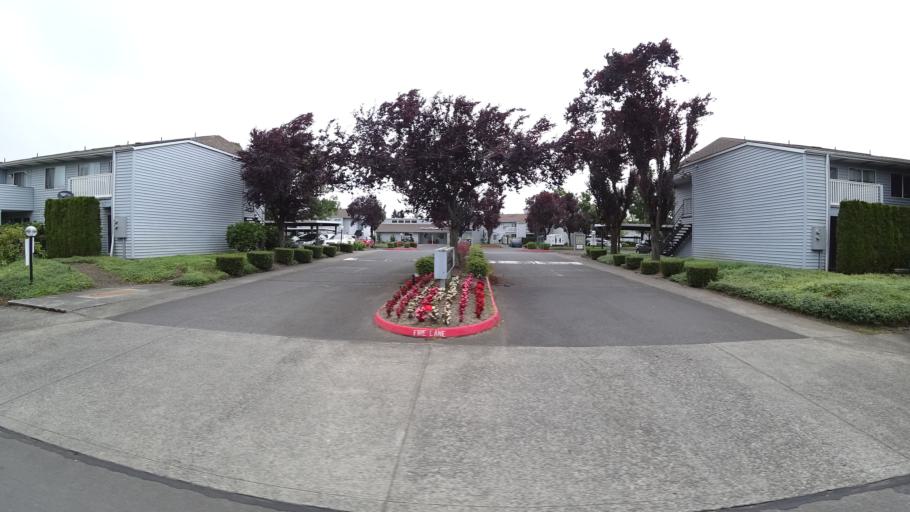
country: US
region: Oregon
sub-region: Multnomah County
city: Fairview
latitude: 45.5407
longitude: -122.4908
